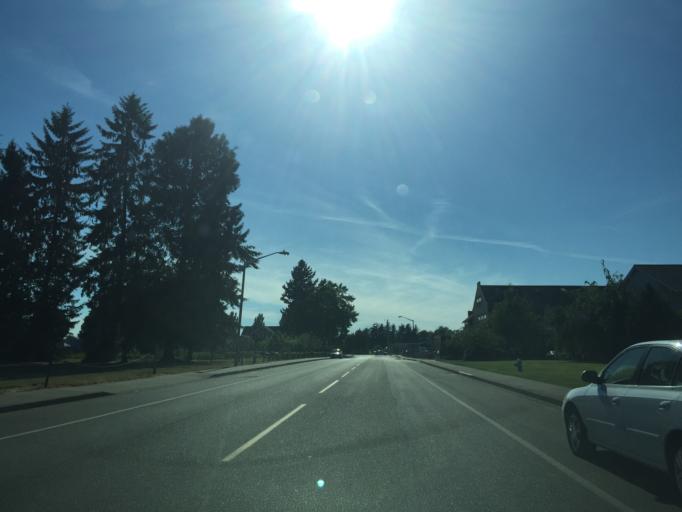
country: US
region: Washington
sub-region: Whatcom County
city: Lynden
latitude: 48.9625
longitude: -122.4385
